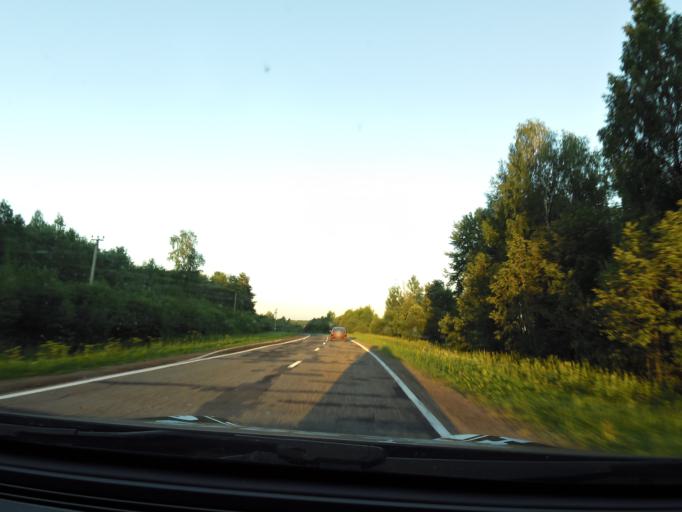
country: RU
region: Jaroslavl
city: Prechistoye
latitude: 58.3628
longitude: 40.4975
